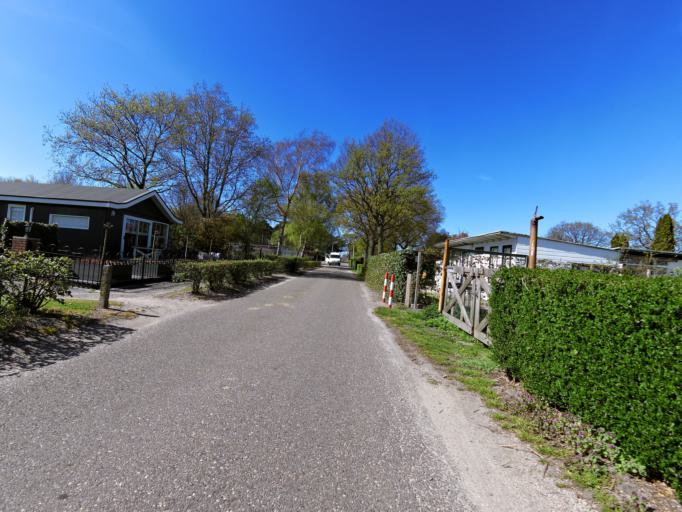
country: NL
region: South Holland
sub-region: Gemeente Brielle
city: Brielle
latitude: 51.9224
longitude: 4.1188
